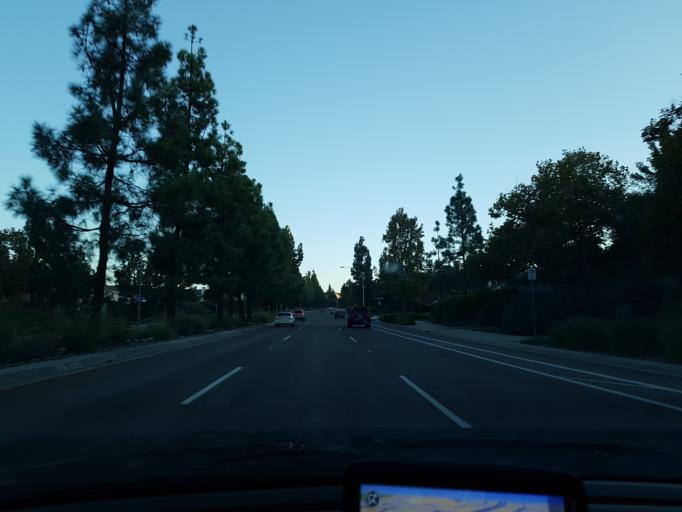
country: US
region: California
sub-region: San Diego County
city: Fairbanks Ranch
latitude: 32.9276
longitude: -117.1251
